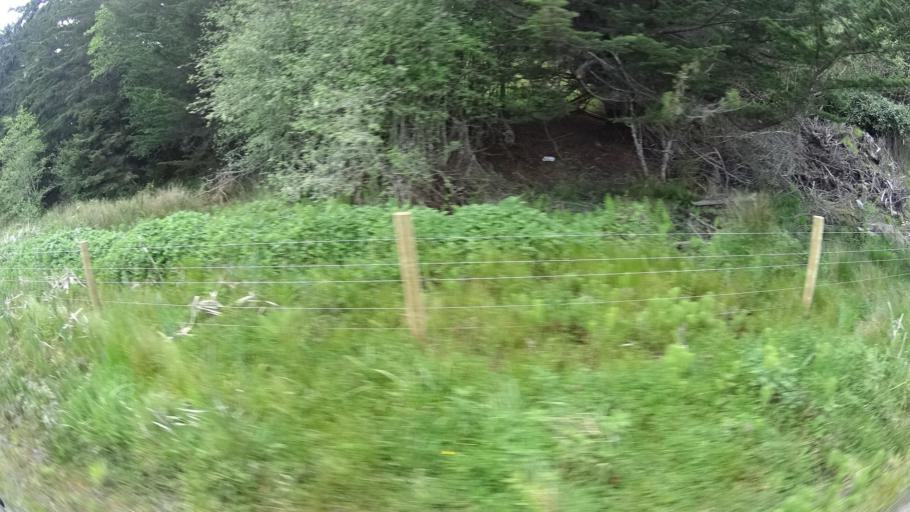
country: US
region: California
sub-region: Humboldt County
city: Humboldt Hill
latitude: 40.6837
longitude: -124.2317
